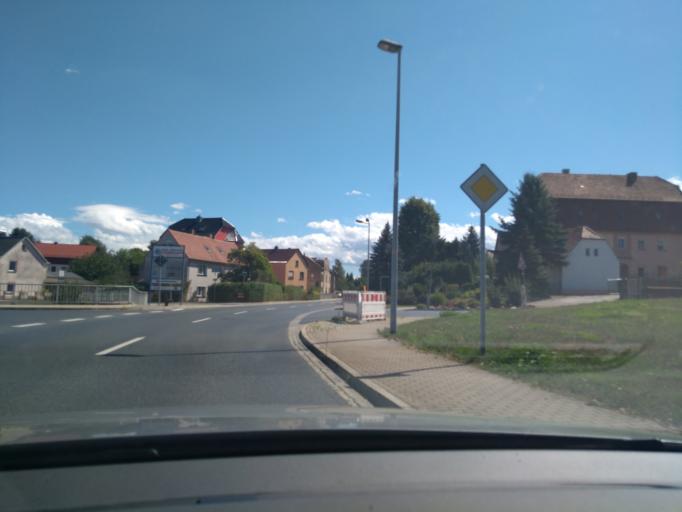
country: DE
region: Saxony
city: Grossrohrsdorf
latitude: 51.1447
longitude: 14.0315
